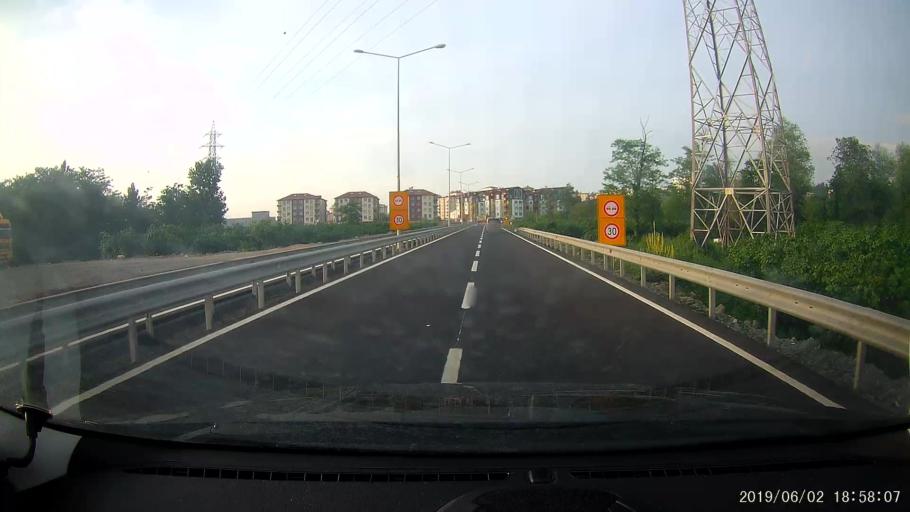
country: TR
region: Ordu
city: Ordu
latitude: 40.9587
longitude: 37.9078
